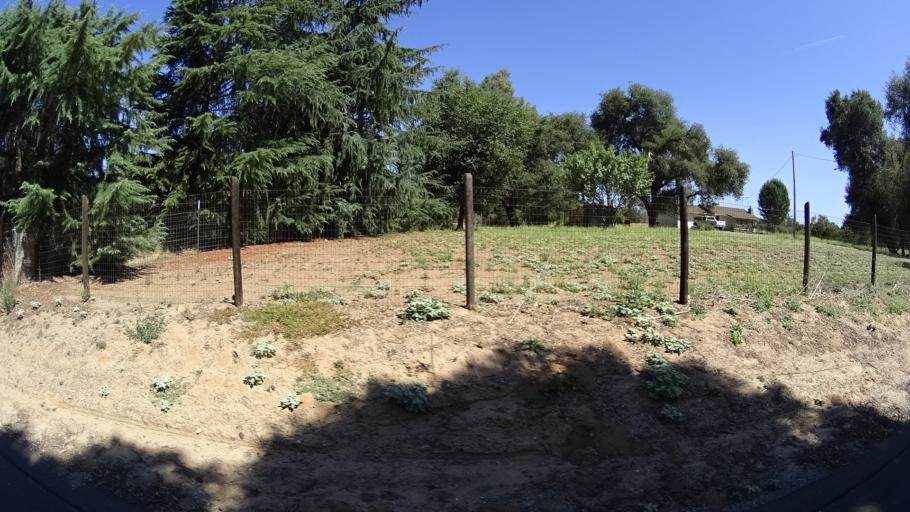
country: US
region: California
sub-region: Calaveras County
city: Rancho Calaveras
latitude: 38.1822
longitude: -120.9026
